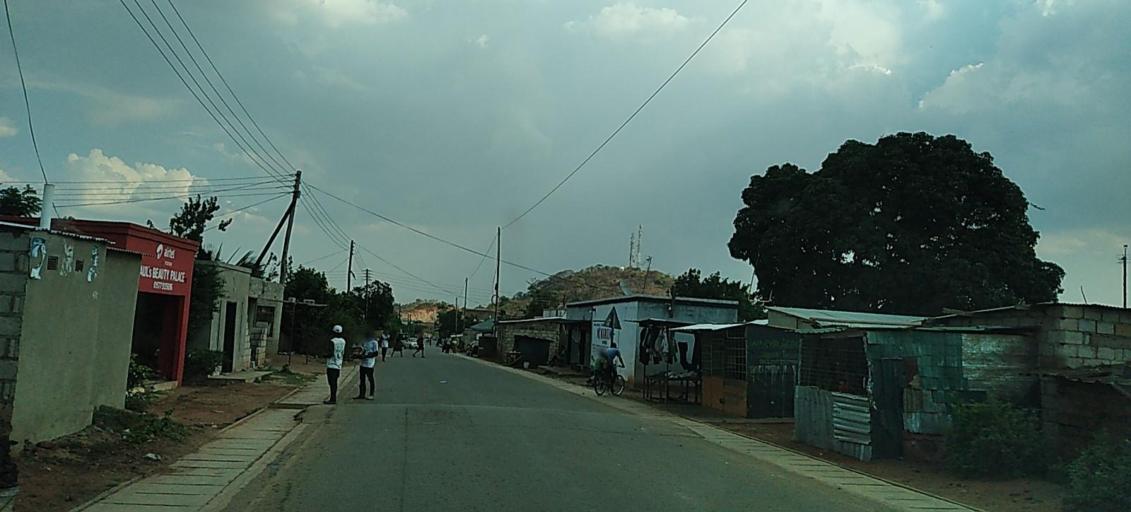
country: ZM
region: Lusaka
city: Lusaka
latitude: -15.5370
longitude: 28.2377
